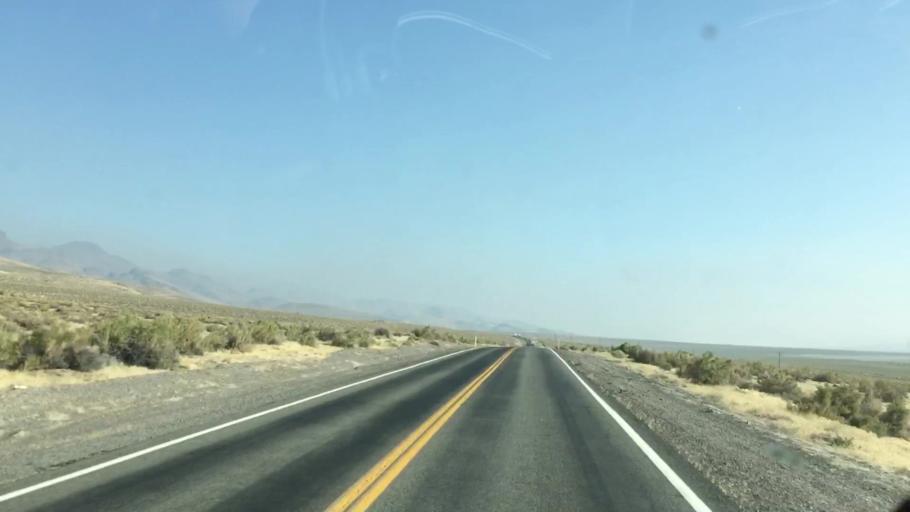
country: US
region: Nevada
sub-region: Lyon County
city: Fernley
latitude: 39.9763
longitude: -119.3838
